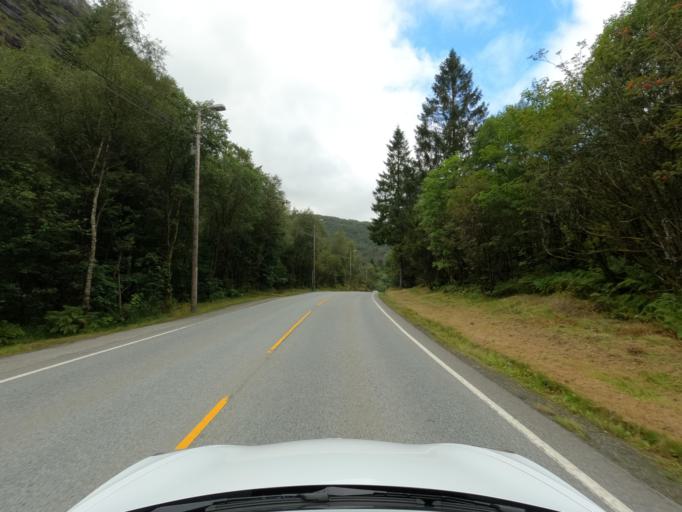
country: NO
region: Hordaland
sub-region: Bergen
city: Espeland
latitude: 60.3530
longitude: 5.4492
